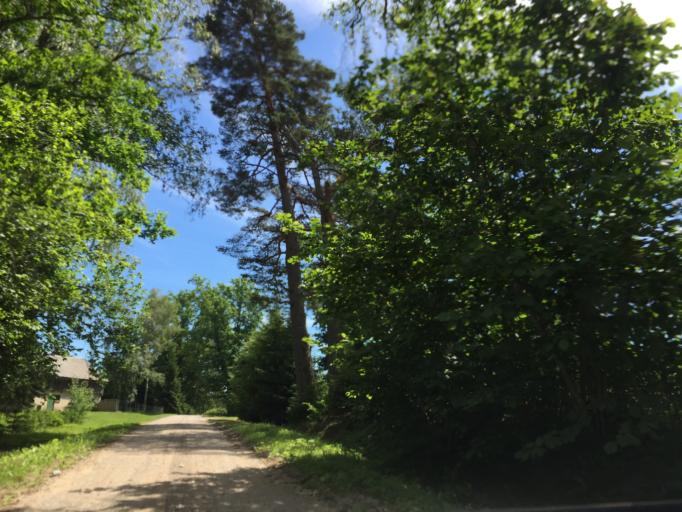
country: LV
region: Kuldigas Rajons
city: Kuldiga
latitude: 57.1188
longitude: 21.8721
